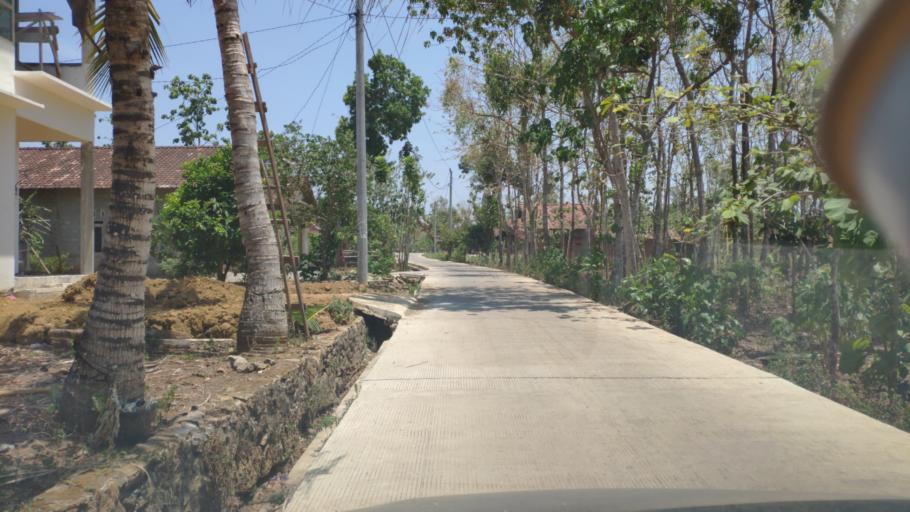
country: ID
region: Central Java
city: Ngapus
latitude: -6.9529
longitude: 111.1794
